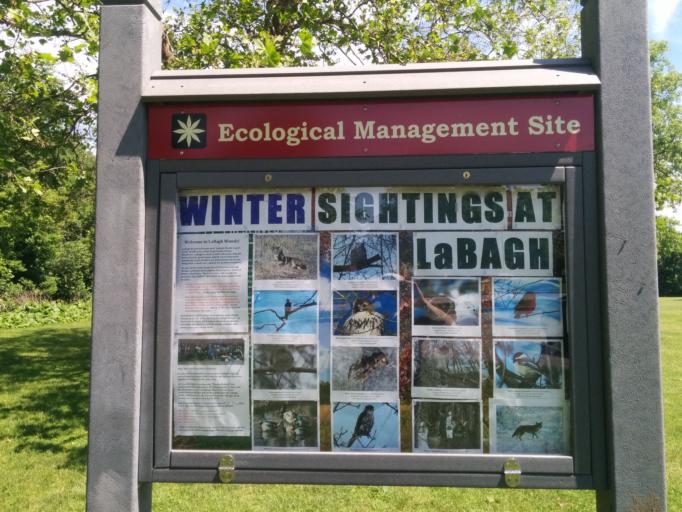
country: US
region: Illinois
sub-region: Cook County
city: Lincolnwood
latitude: 41.9762
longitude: -87.7412
